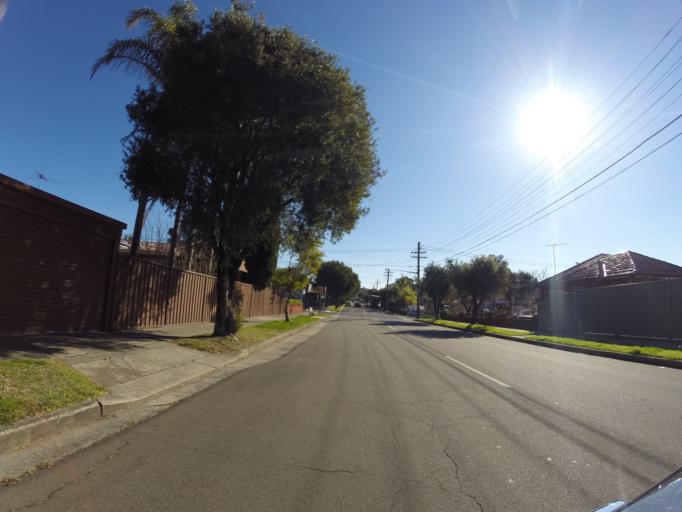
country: AU
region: New South Wales
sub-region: Auburn
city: Lidcombe
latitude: -33.8567
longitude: 151.0516
